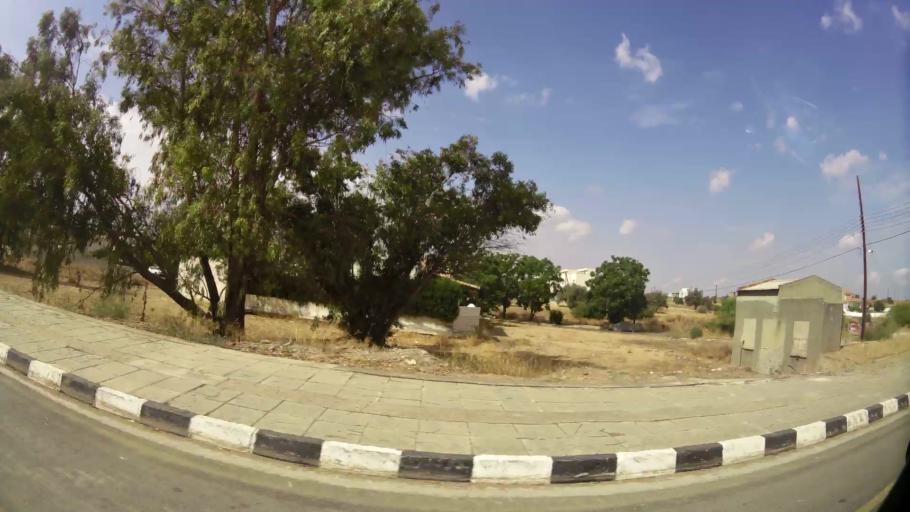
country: CY
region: Lefkosia
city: Tseri
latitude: 35.0797
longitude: 33.3260
